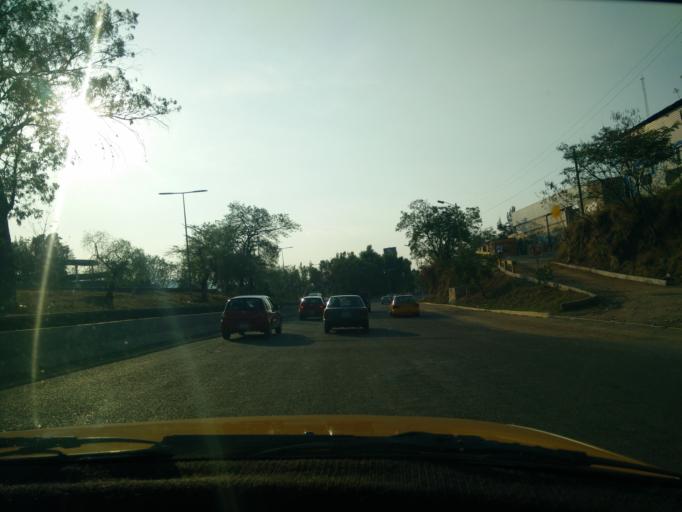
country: MX
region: Oaxaca
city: Oaxaca de Juarez
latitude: 17.0803
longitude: -96.7419
